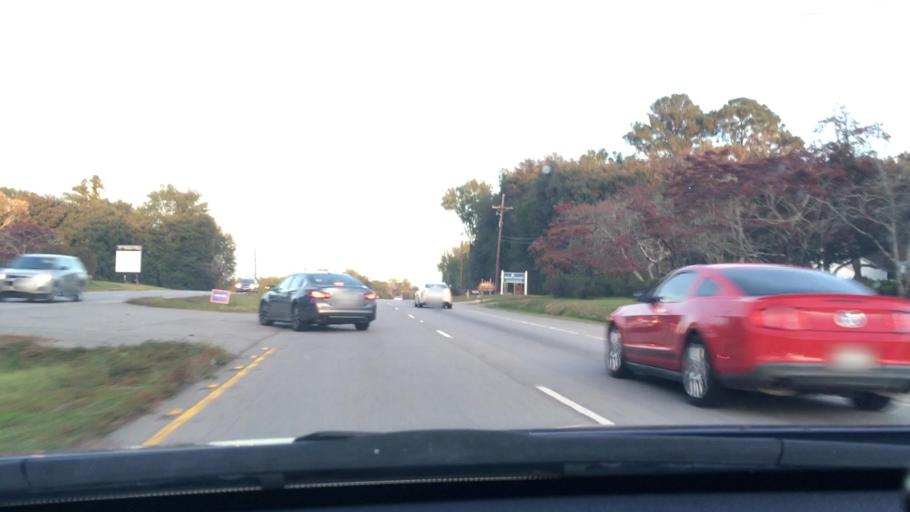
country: US
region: South Carolina
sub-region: Richland County
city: Hopkins
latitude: 33.9443
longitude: -80.8938
